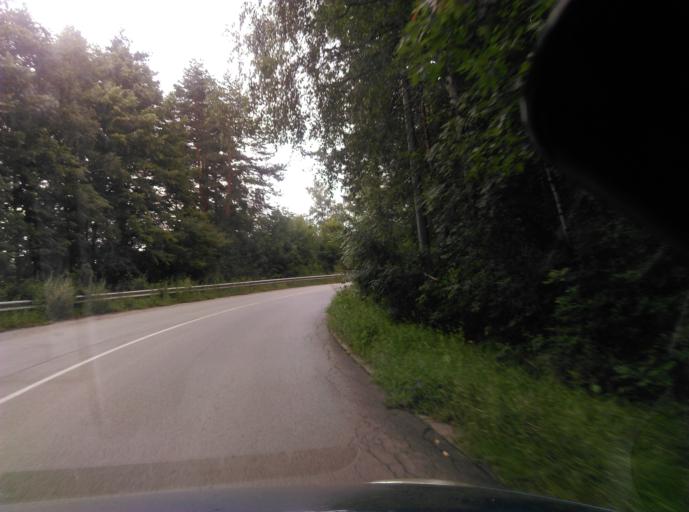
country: BG
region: Sofia-Capital
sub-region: Stolichna Obshtina
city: Sofia
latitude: 42.6052
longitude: 23.3509
